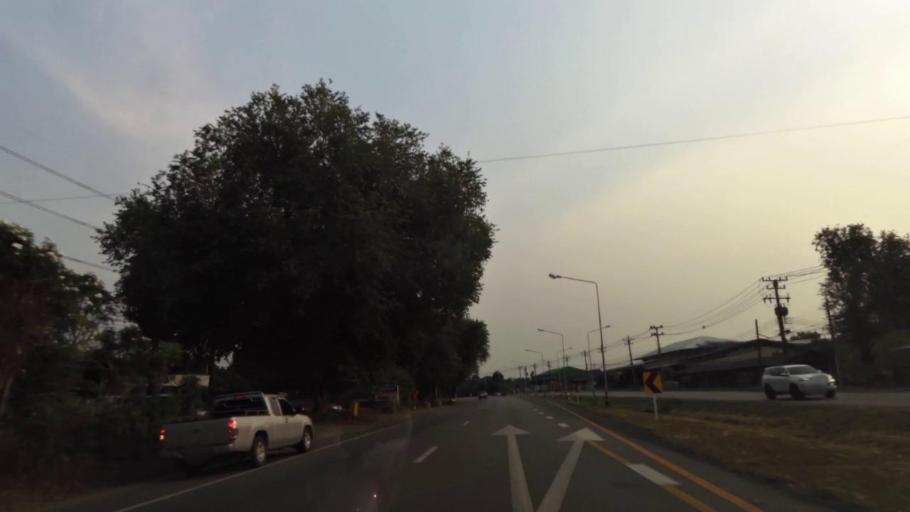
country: TH
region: Chanthaburi
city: Khlung
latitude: 12.4893
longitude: 102.1744
